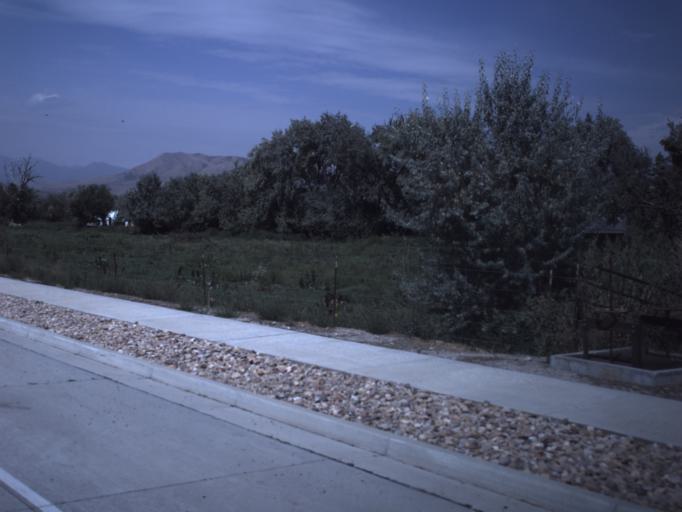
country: US
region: Utah
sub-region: Utah County
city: Saratoga Springs
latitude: 40.3763
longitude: -111.8922
